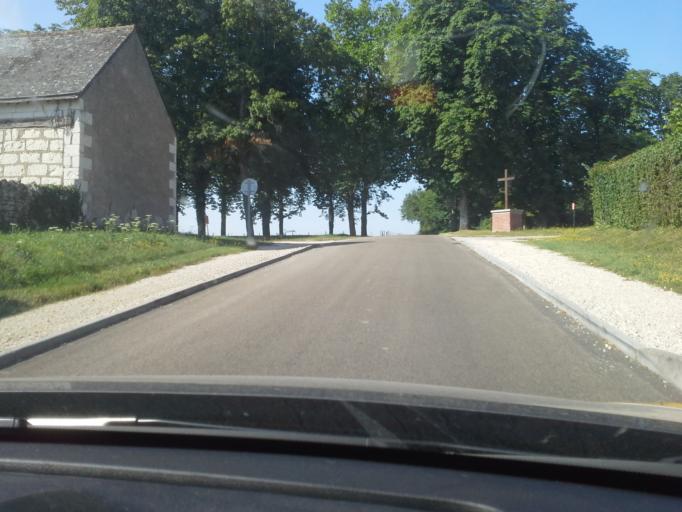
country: FR
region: Centre
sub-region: Departement du Loir-et-Cher
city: Chaumont-sur-Loire
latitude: 47.4756
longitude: 1.1894
